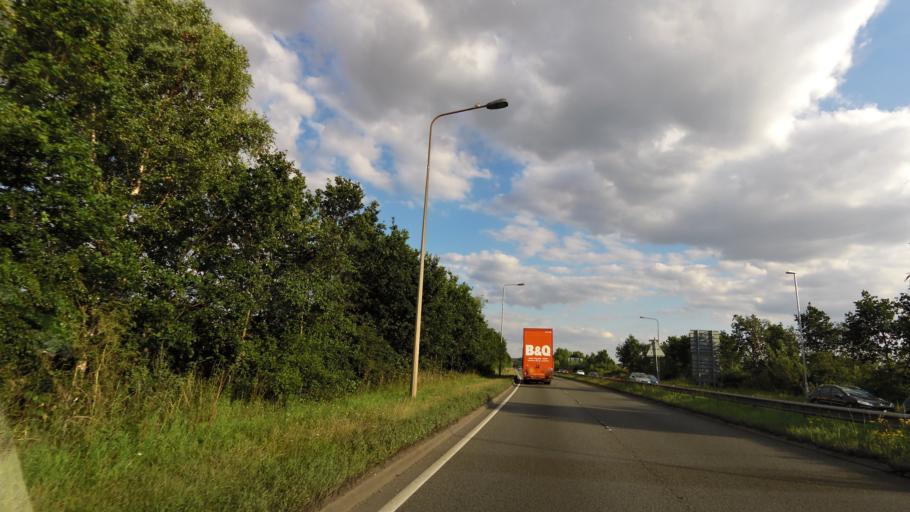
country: GB
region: England
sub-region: Nottinghamshire
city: Worksop
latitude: 53.3099
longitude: -1.1416
